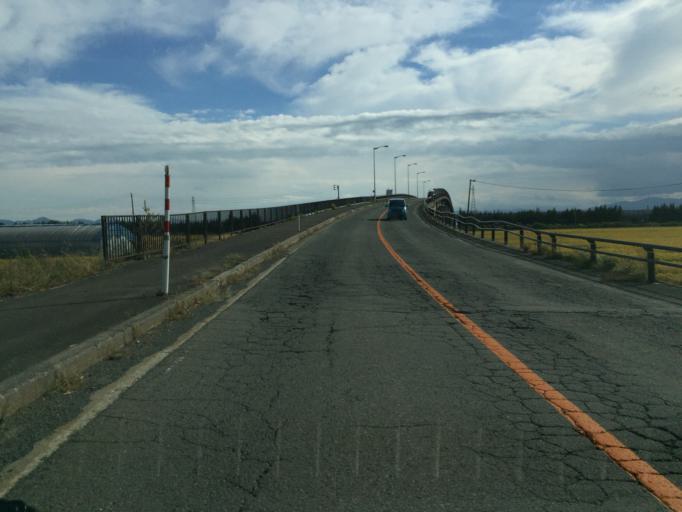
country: JP
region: Fukushima
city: Inawashiro
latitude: 37.5523
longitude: 140.0790
